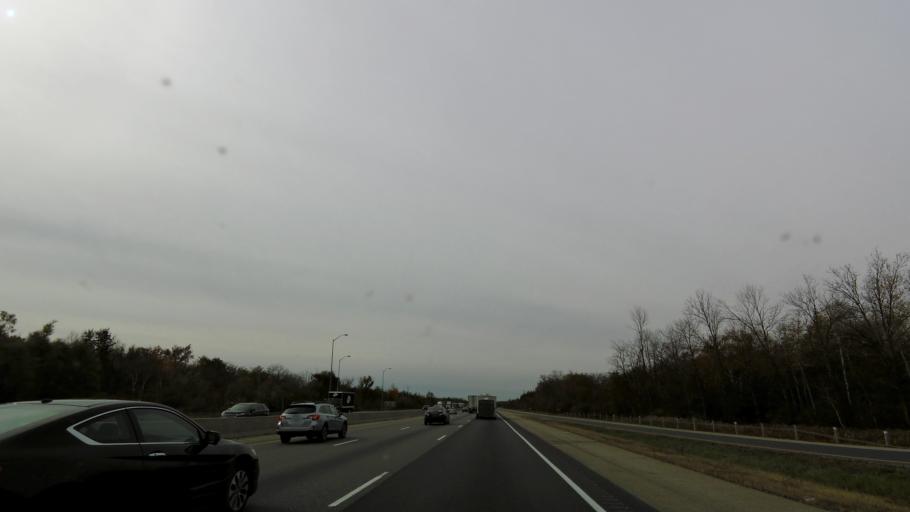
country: CA
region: Ontario
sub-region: Wellington County
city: Guelph
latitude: 43.4474
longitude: -80.1797
